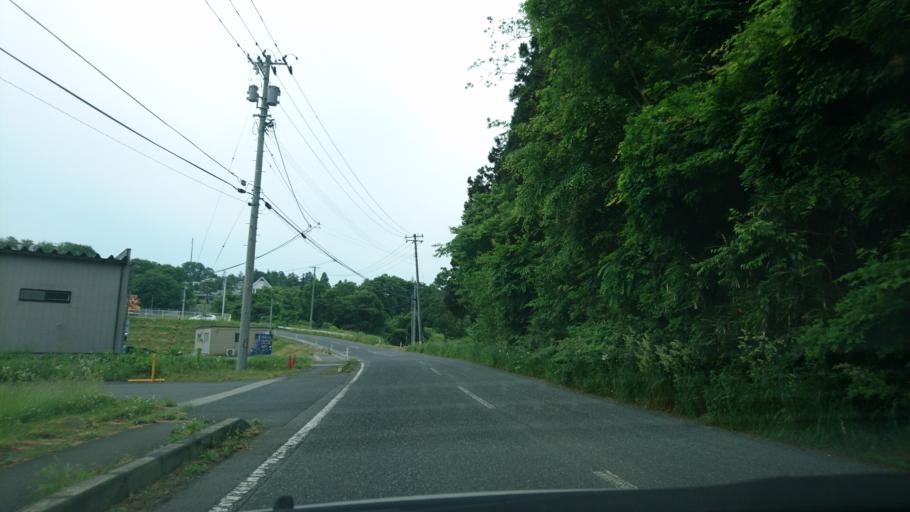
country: JP
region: Iwate
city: Ichinoseki
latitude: 38.8838
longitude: 141.1366
